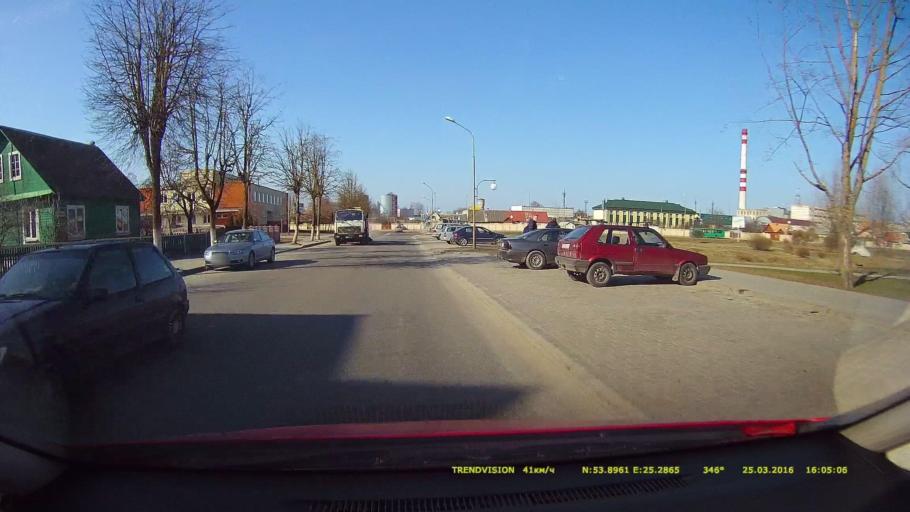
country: BY
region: Grodnenskaya
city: Lida
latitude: 53.8962
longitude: 25.2864
